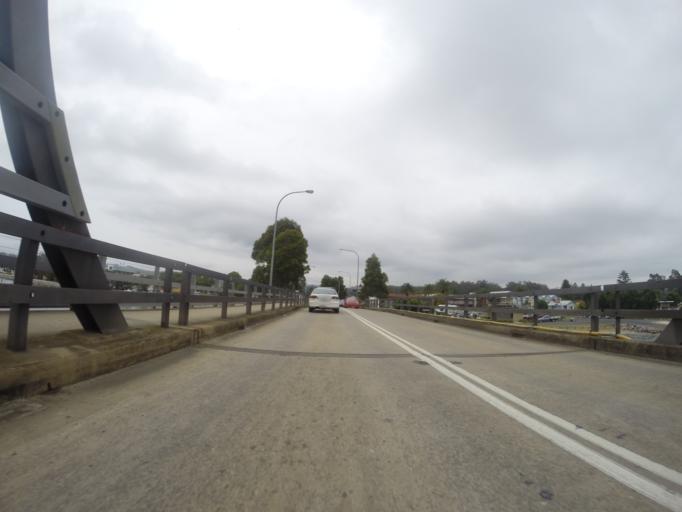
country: AU
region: New South Wales
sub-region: Eurobodalla
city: Batemans Bay
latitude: -35.7024
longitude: 150.1787
